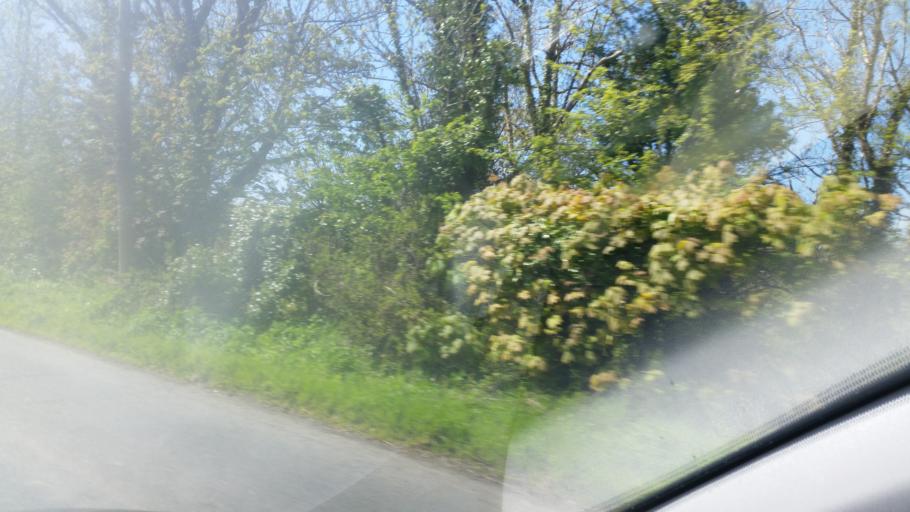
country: IE
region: Munster
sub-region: Waterford
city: Dunmore East
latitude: 52.2100
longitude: -6.8591
